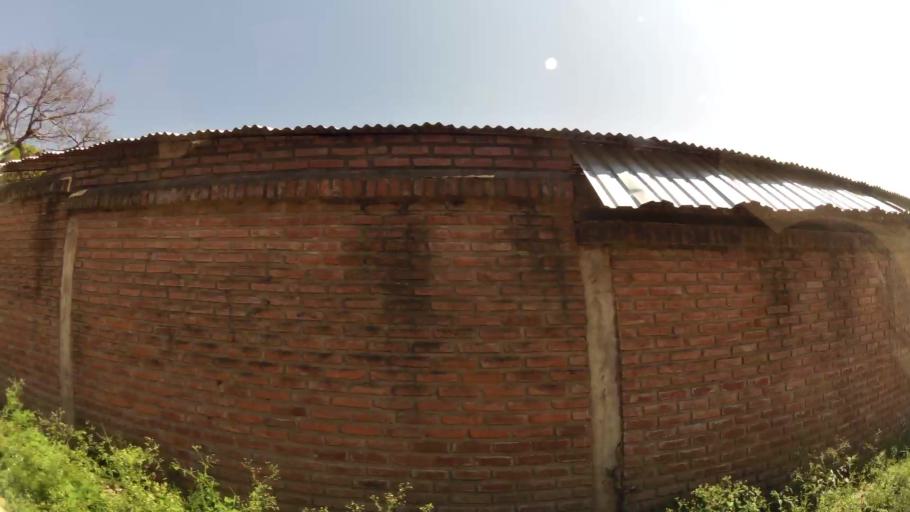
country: BO
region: Santa Cruz
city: Santa Cruz de la Sierra
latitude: -17.7460
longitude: -63.1813
